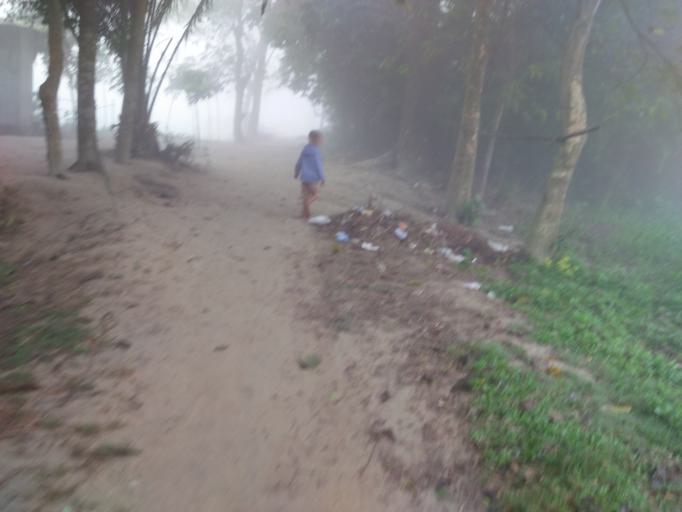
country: BD
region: Dhaka
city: Azimpur
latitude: 23.6877
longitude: 90.2978
